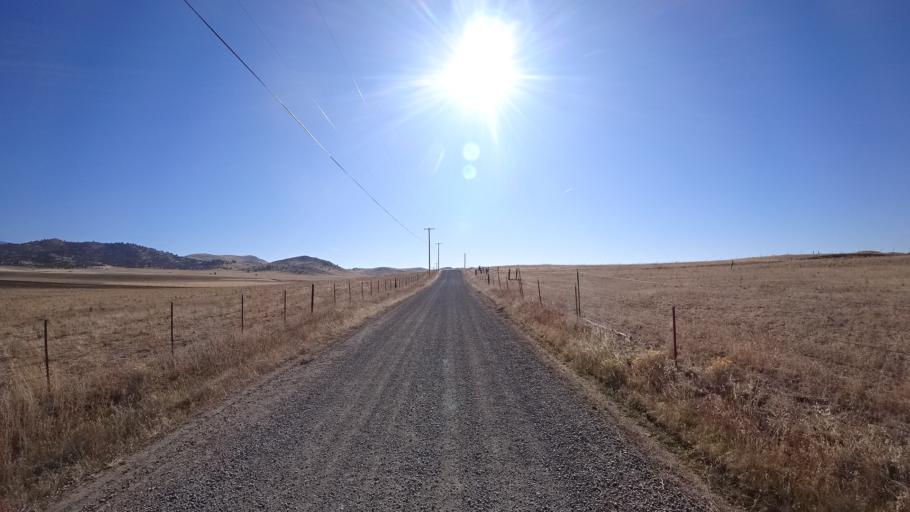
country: US
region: California
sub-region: Siskiyou County
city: Montague
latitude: 41.8019
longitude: -122.4159
